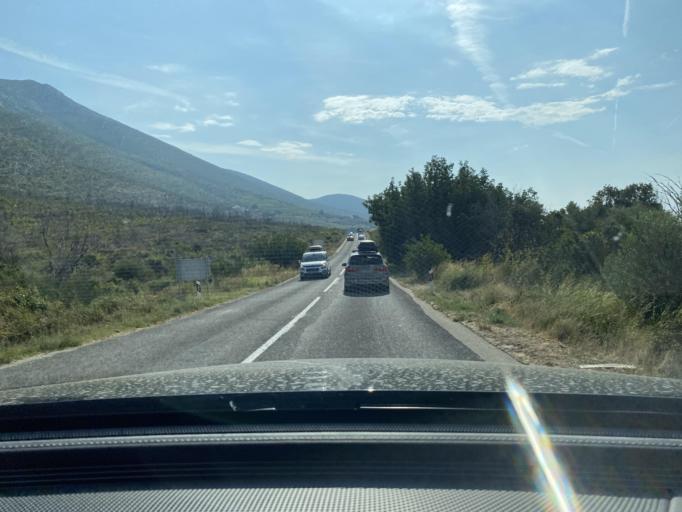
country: HR
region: Dubrovacko-Neretvanska
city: Orebic
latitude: 42.9830
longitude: 17.2089
